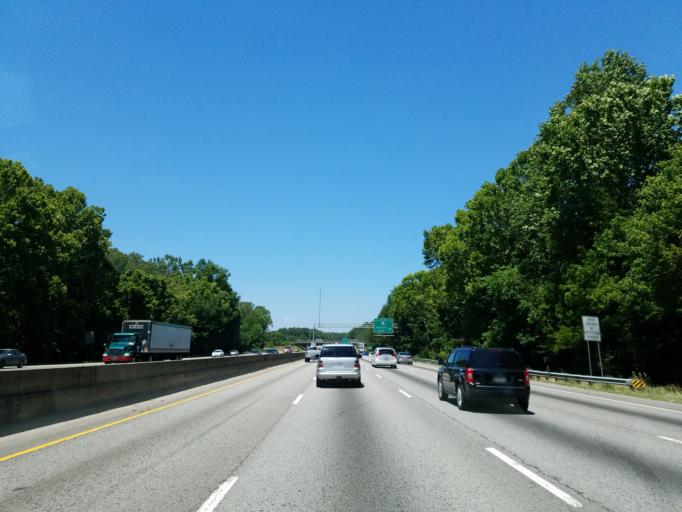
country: US
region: Georgia
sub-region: Clayton County
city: Forest Park
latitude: 33.6483
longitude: -84.3699
